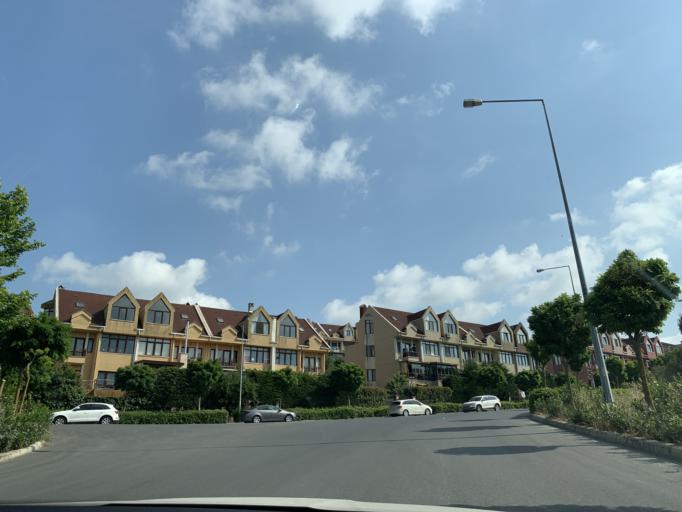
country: TR
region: Istanbul
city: Esenyurt
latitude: 41.0832
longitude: 28.6691
